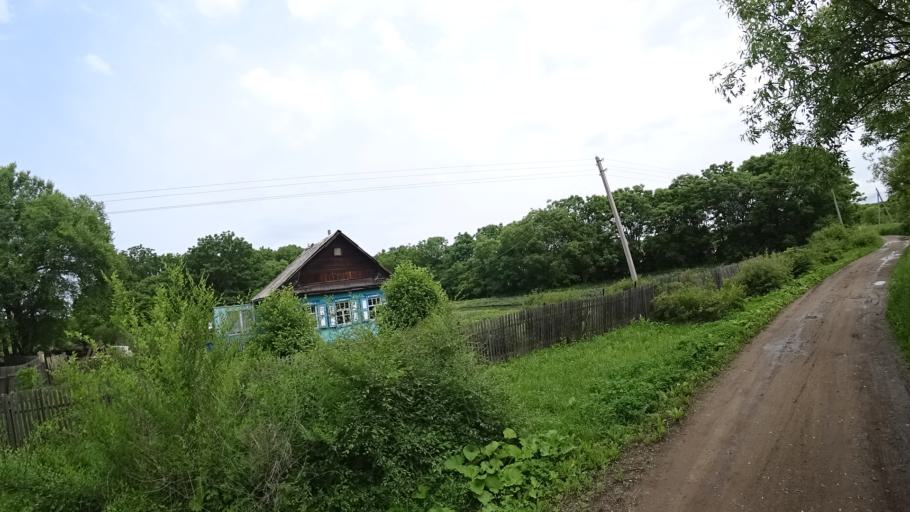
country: RU
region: Primorskiy
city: Novosysoyevka
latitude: 44.2476
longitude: 133.3699
